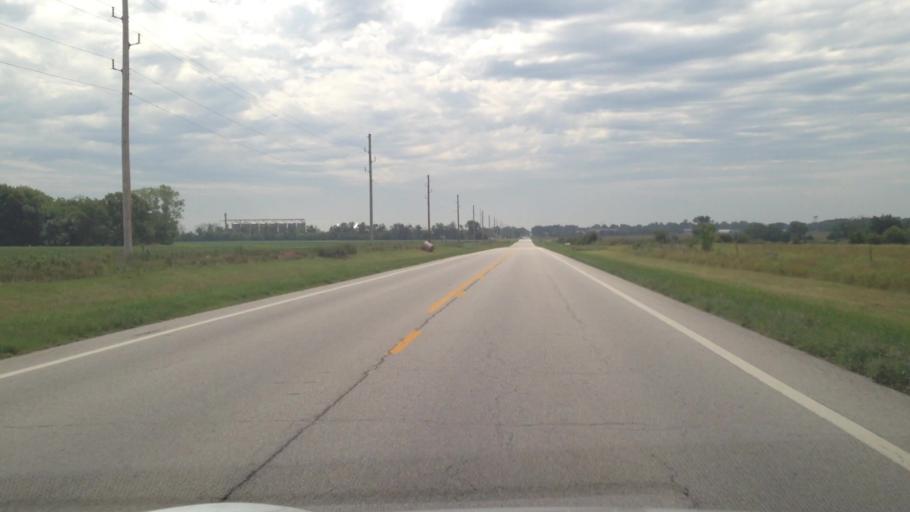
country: US
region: Kansas
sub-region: Allen County
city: Iola
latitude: 37.9352
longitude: -95.1701
